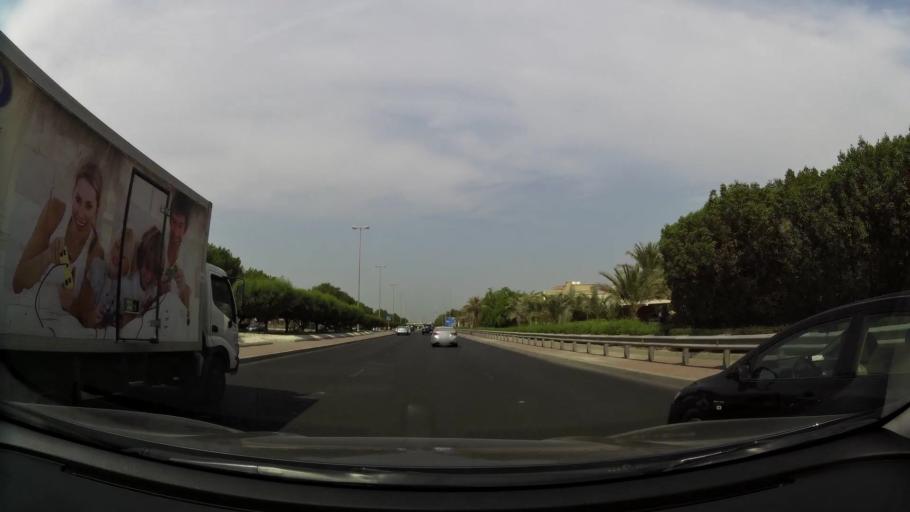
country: KW
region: Muhafazat Hawalli
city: Hawalli
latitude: 29.3148
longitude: 47.9959
